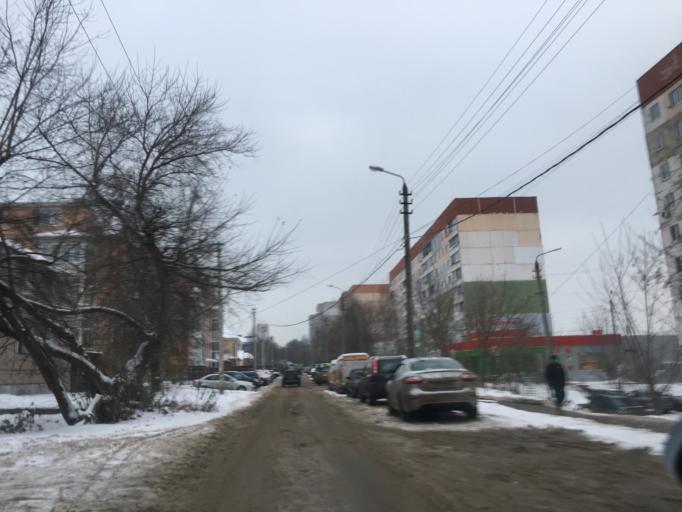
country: RU
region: Tula
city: Tula
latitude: 54.1853
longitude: 37.5683
